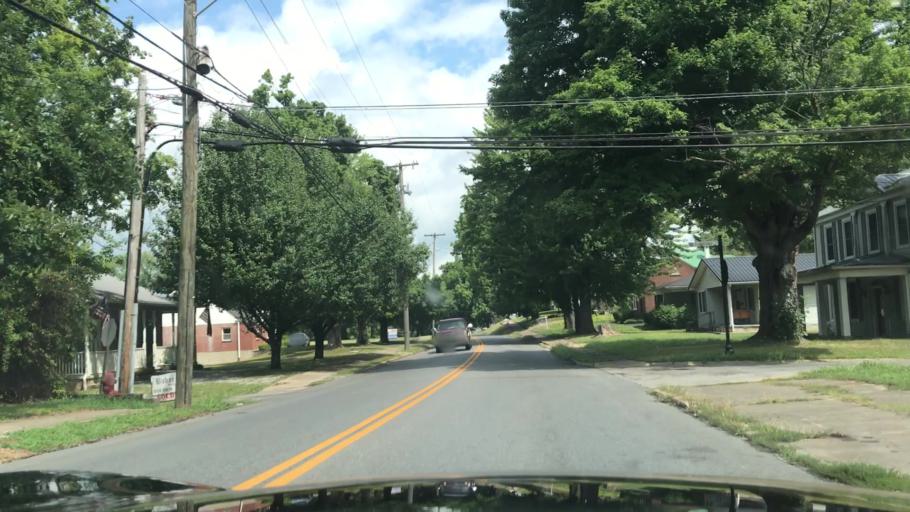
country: US
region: Kentucky
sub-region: Muhlenberg County
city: Greenville
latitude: 37.2052
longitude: -87.1789
